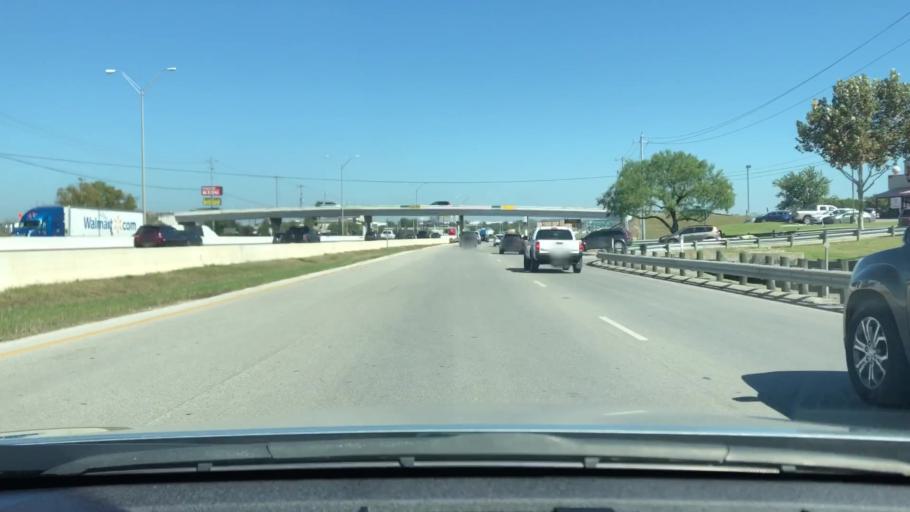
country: US
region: Texas
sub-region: Bexar County
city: Live Oak
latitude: 29.5765
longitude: -98.3225
